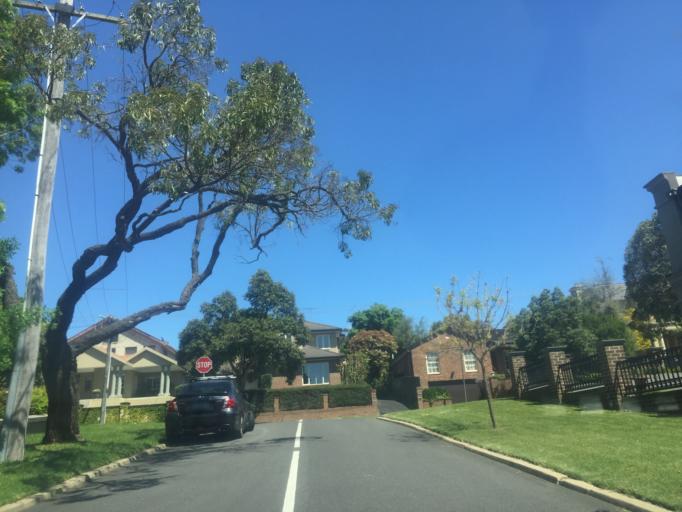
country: AU
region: Victoria
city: Mont Albert
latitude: -37.8073
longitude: 145.0906
